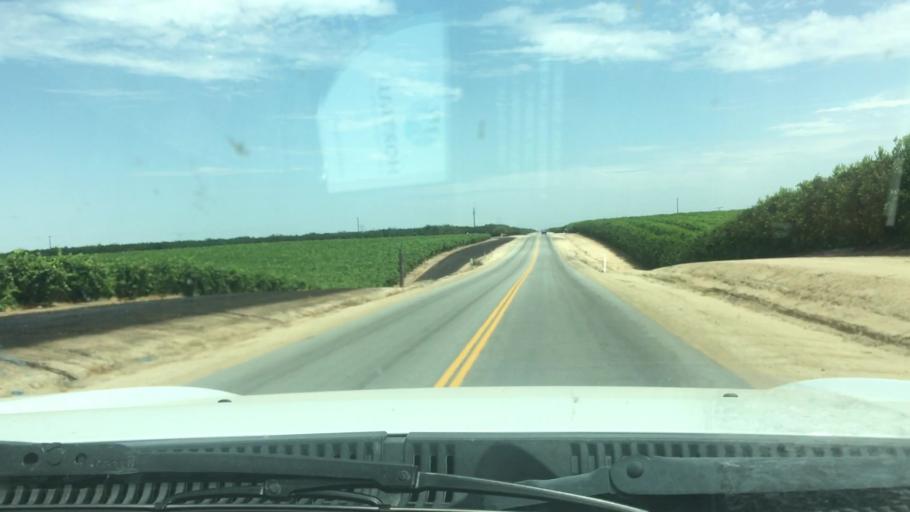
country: US
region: California
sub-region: Kern County
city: McFarland
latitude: 35.5703
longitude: -119.1511
